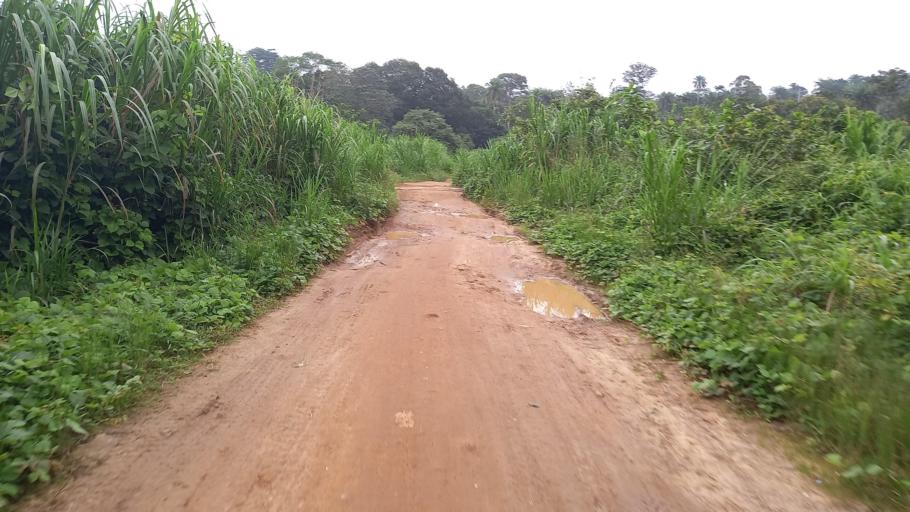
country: SL
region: Eastern Province
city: Kailahun
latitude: 8.2390
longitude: -10.5184
